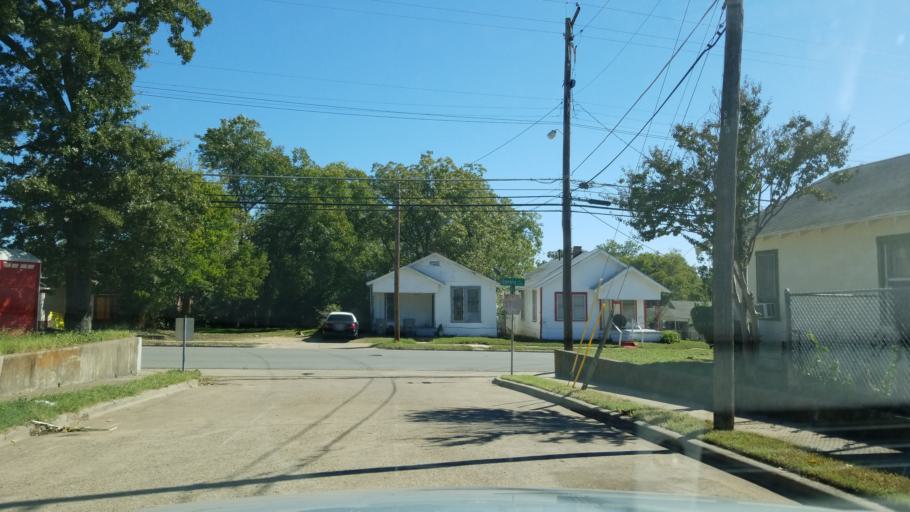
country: US
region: Texas
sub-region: Dallas County
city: Dallas
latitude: 32.7733
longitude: -96.7445
